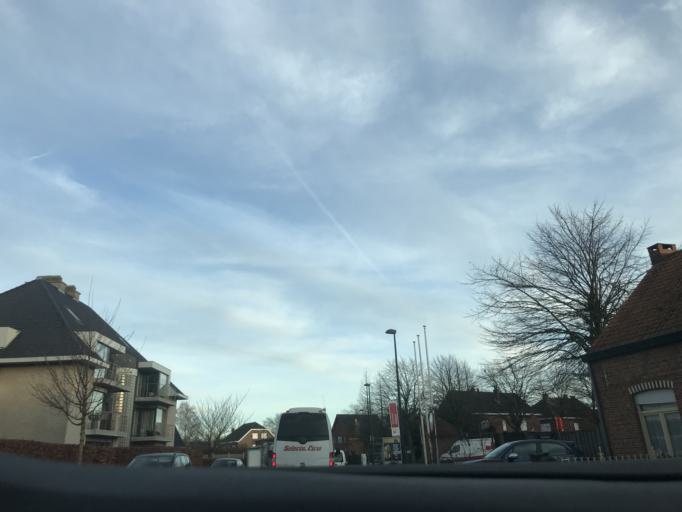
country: BE
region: Flanders
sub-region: Provincie Oost-Vlaanderen
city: Destelbergen
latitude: 51.0939
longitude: 3.7640
